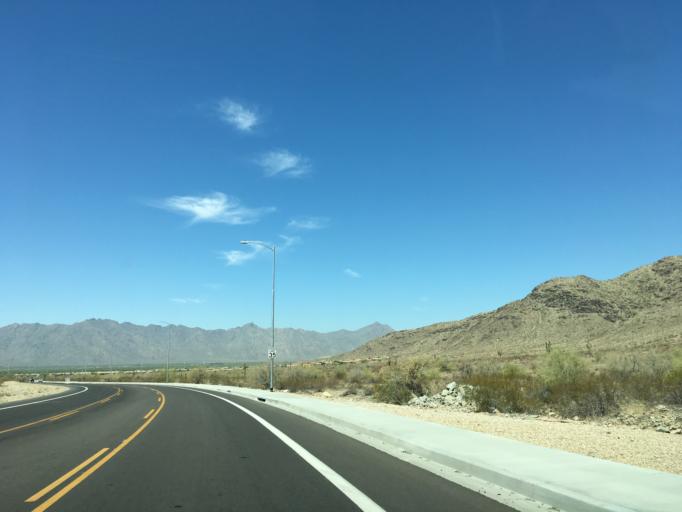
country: US
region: Arizona
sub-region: Maricopa County
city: Laveen
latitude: 33.3028
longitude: -112.1037
